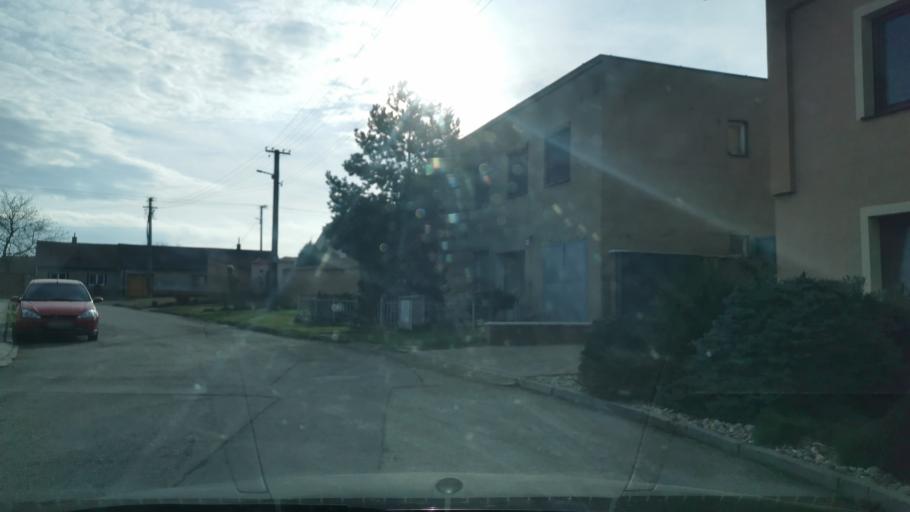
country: SK
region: Trnavsky
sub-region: Okres Skalica
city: Holic
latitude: 48.7874
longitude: 17.1060
